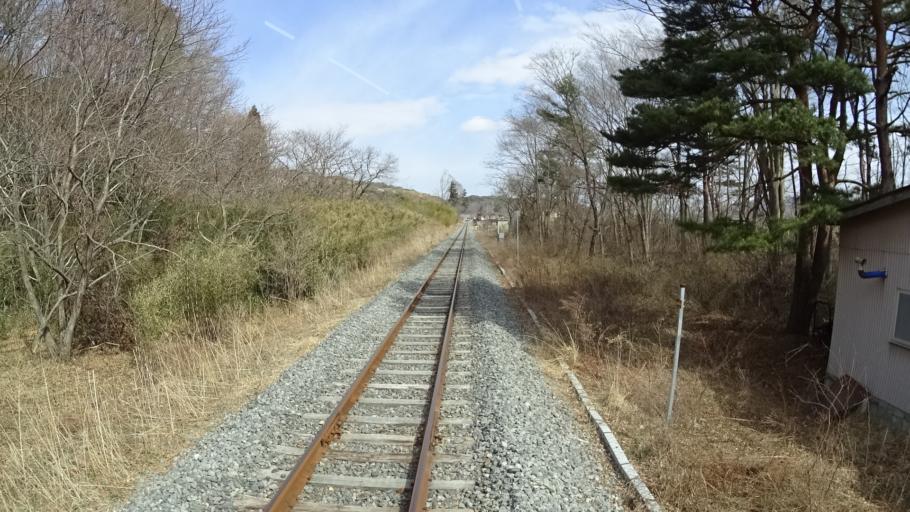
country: JP
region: Iwate
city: Miyako
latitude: 39.5709
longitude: 141.9325
